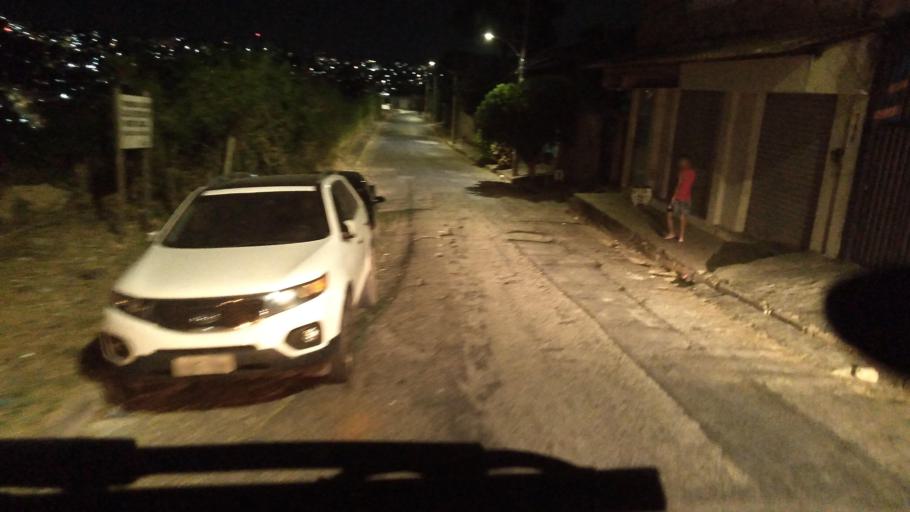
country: BR
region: Minas Gerais
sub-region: Belo Horizonte
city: Belo Horizonte
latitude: -19.8858
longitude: -43.9554
